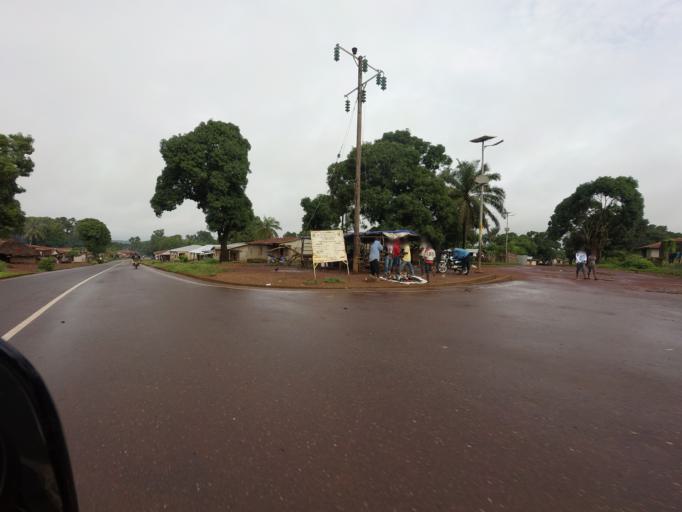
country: SL
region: Northern Province
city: Kambia
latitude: 9.1280
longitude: -12.9081
